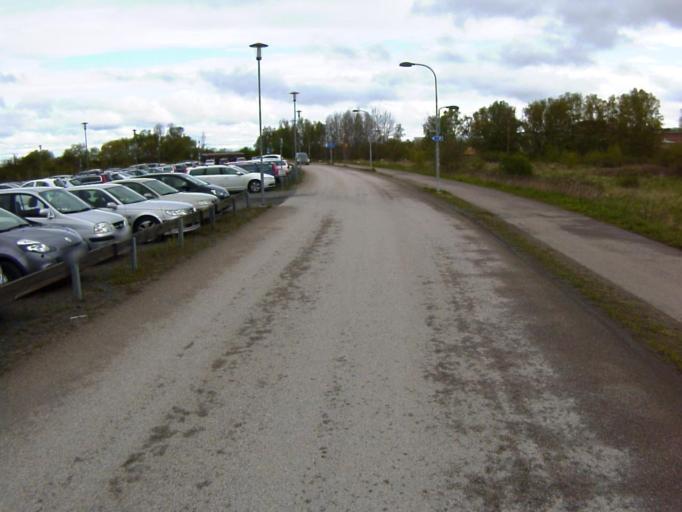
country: SE
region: Skane
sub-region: Kristianstads Kommun
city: Kristianstad
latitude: 56.0268
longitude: 14.1456
